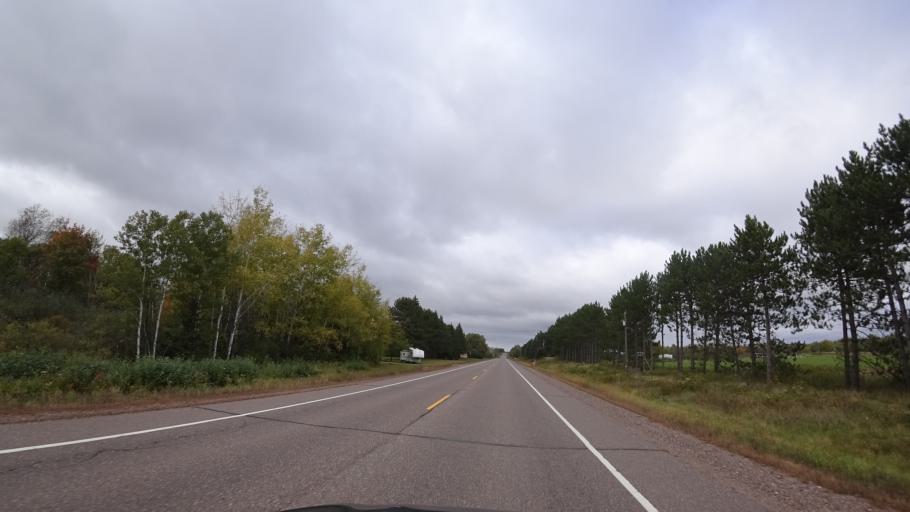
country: US
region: Wisconsin
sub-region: Rusk County
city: Ladysmith
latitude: 45.5245
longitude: -91.1115
